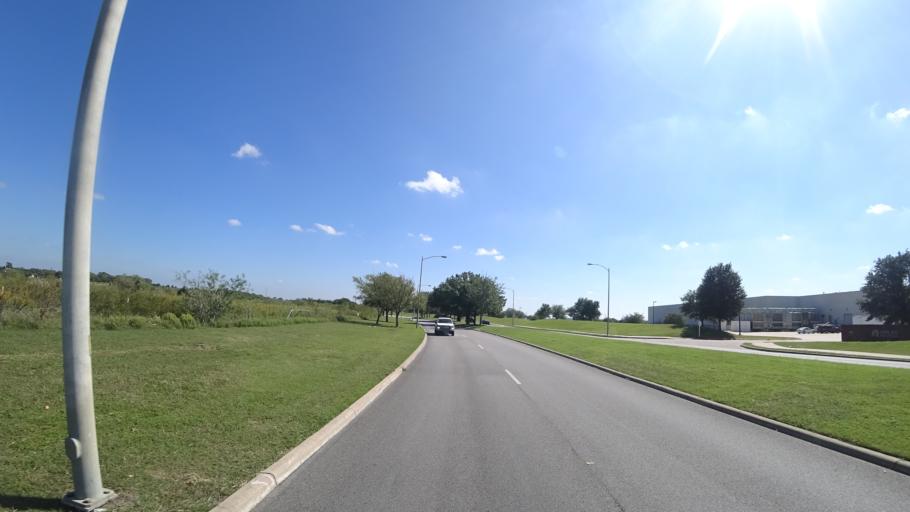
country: US
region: Texas
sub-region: Travis County
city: Manor
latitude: 30.3408
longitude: -97.6129
